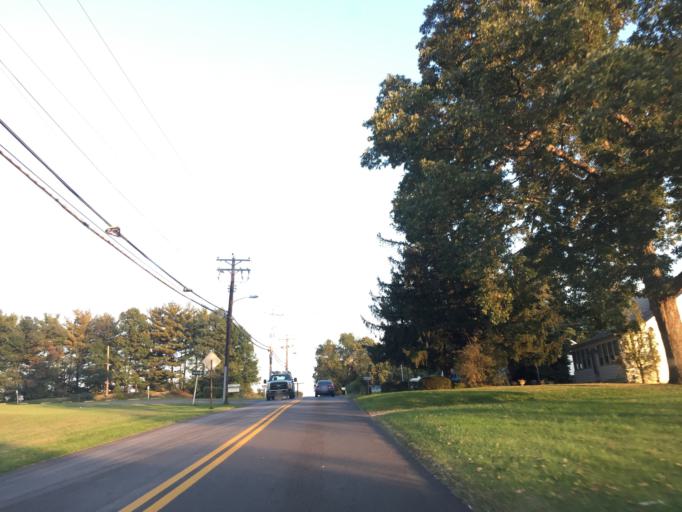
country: US
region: Maryland
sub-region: Baltimore County
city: Essex
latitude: 39.3183
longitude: -76.4637
